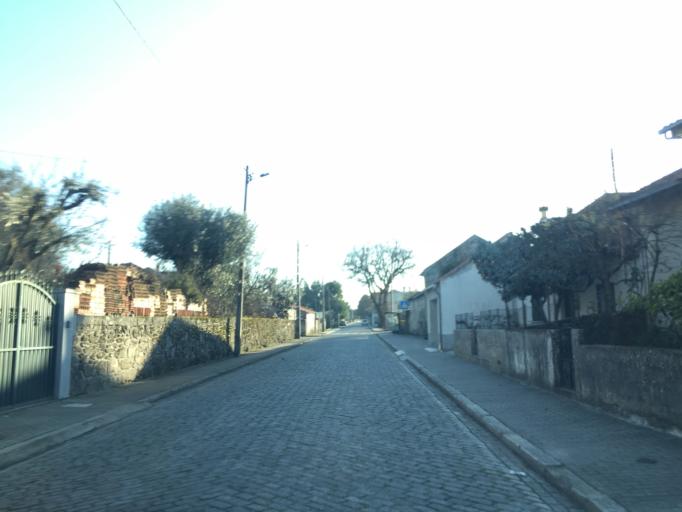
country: PT
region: Viseu
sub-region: Nelas
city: Nelas
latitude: 40.4751
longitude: -7.9188
